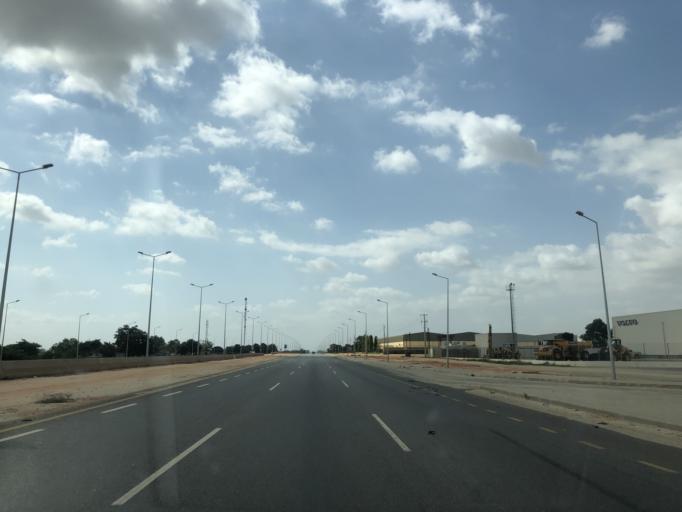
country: AO
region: Luanda
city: Luanda
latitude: -8.9884
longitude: 13.5027
